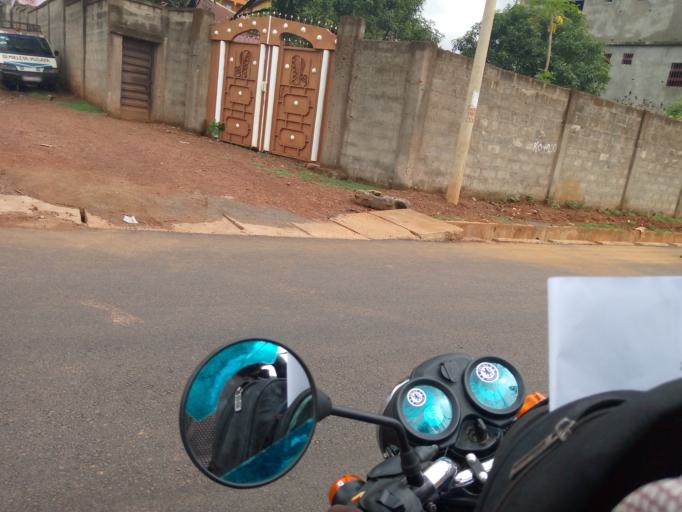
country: SL
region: Western Area
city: Hastings
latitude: 8.4097
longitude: -13.1433
